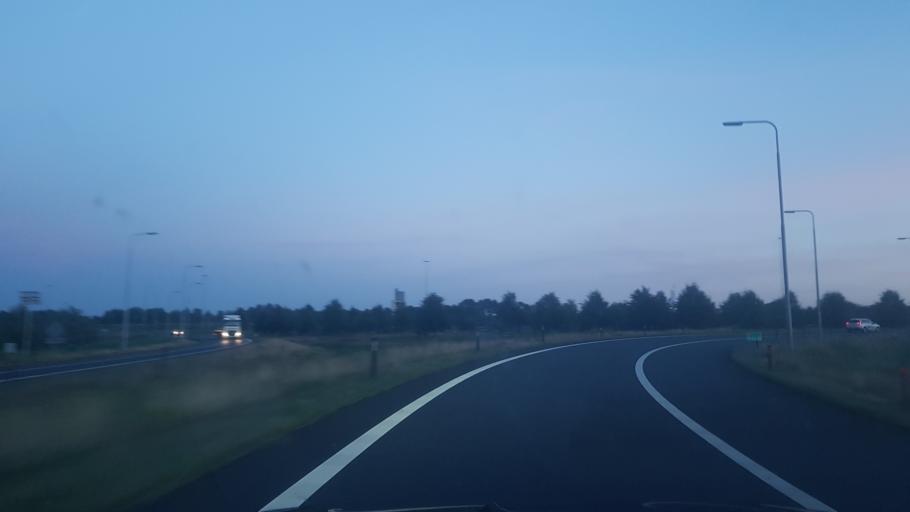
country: NL
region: Friesland
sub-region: Gemeente Heerenveen
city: Heerenveen
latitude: 52.9753
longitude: 5.9205
